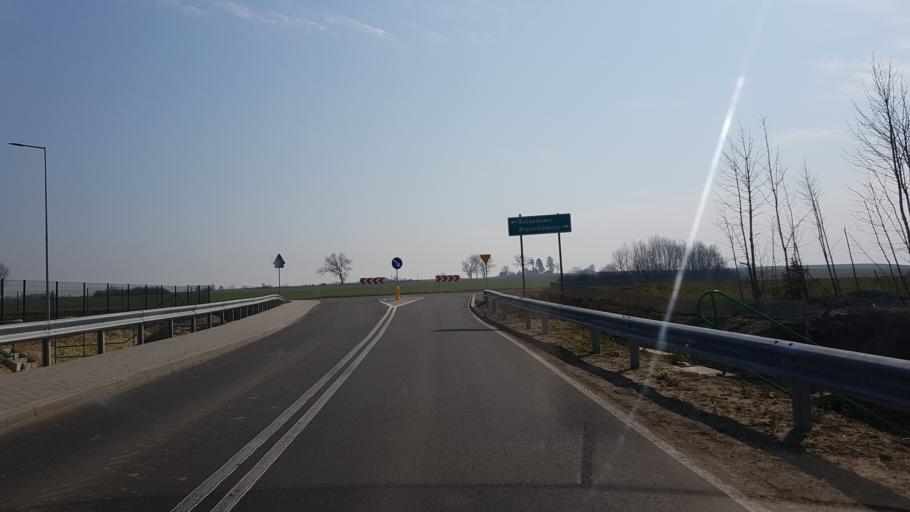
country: PL
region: West Pomeranian Voivodeship
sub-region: Powiat koszalinski
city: Mielno
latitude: 54.1916
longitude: 16.0457
